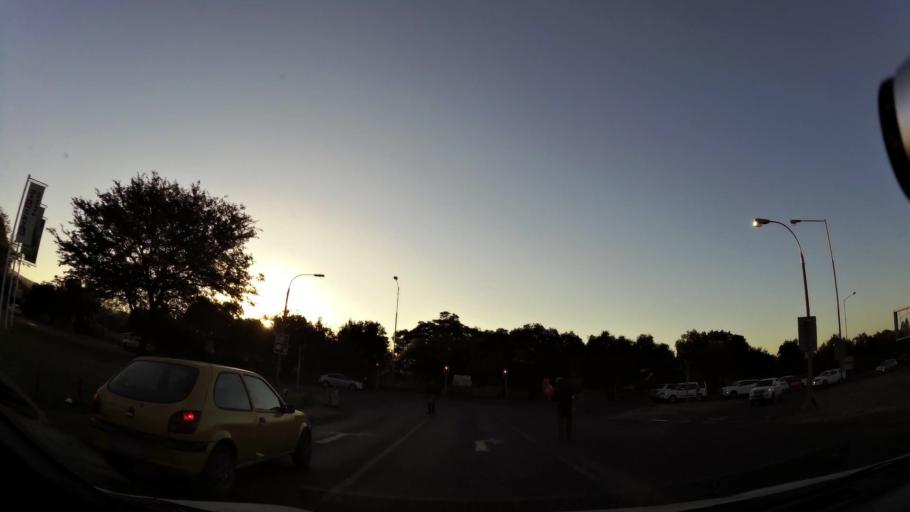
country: ZA
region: North-West
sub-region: Bojanala Platinum District Municipality
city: Rustenburg
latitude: -25.6923
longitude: 27.2241
